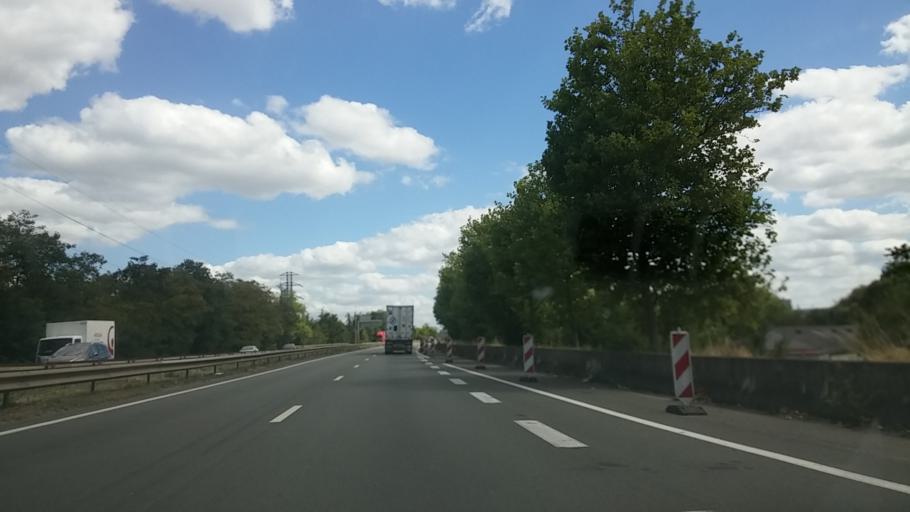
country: FR
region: Ile-de-France
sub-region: Departement des Yvelines
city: Saint-Cyr-l'Ecole
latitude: 48.7941
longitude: 2.0504
